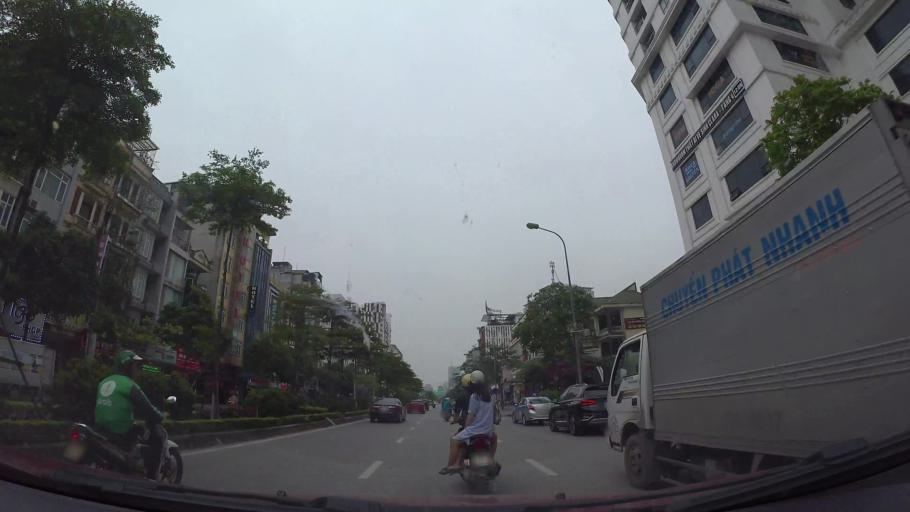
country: VN
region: Ha Noi
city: Cau Giay
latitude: 21.0205
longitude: 105.7917
